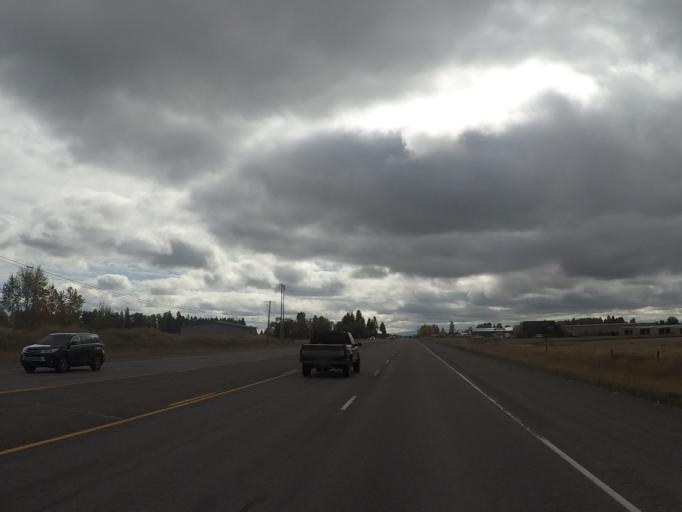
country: US
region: Montana
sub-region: Flathead County
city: Columbia Falls
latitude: 48.3650
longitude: -114.2411
